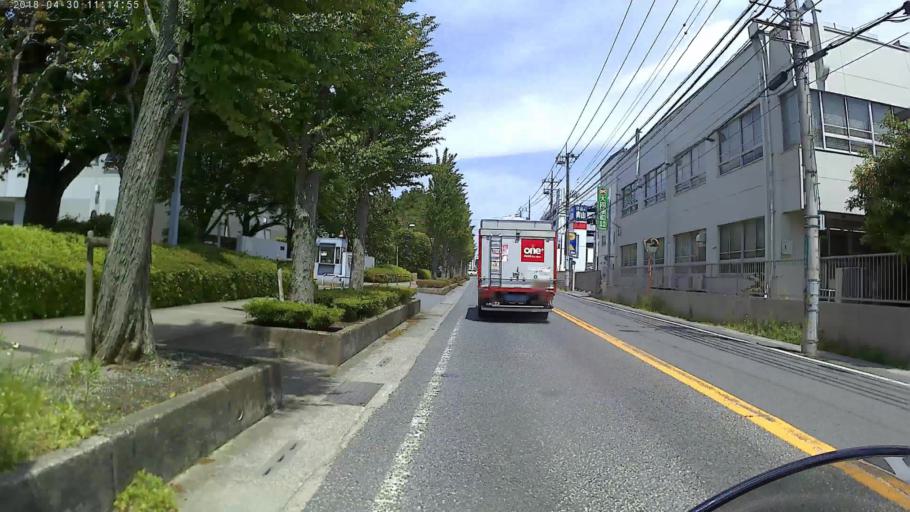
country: JP
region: Kanagawa
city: Minami-rinkan
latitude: 35.4774
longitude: 139.4316
